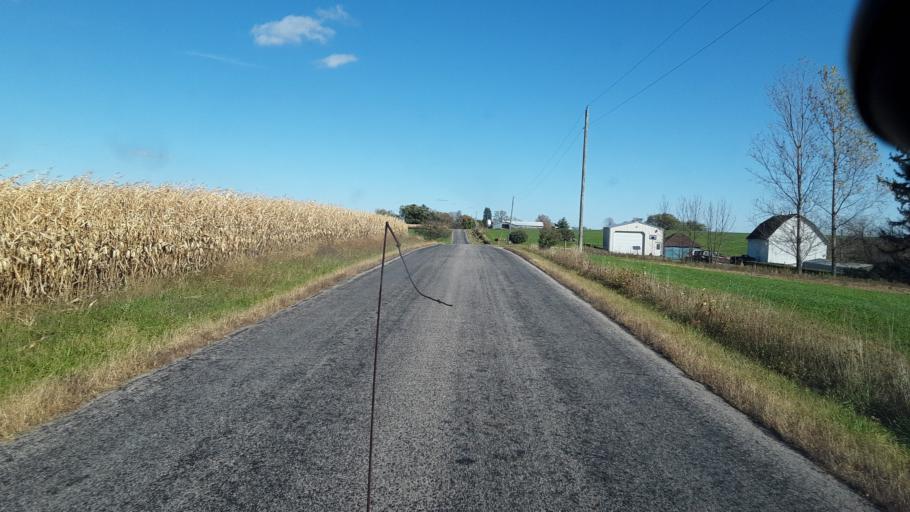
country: US
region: Wisconsin
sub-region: Vernon County
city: Hillsboro
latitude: 43.6858
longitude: -90.4150
